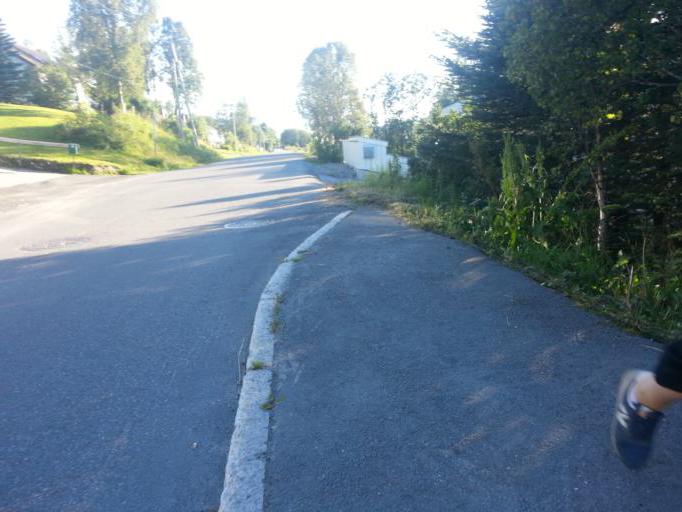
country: NO
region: Troms
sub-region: Tromso
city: Tromso
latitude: 69.6407
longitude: 18.9813
